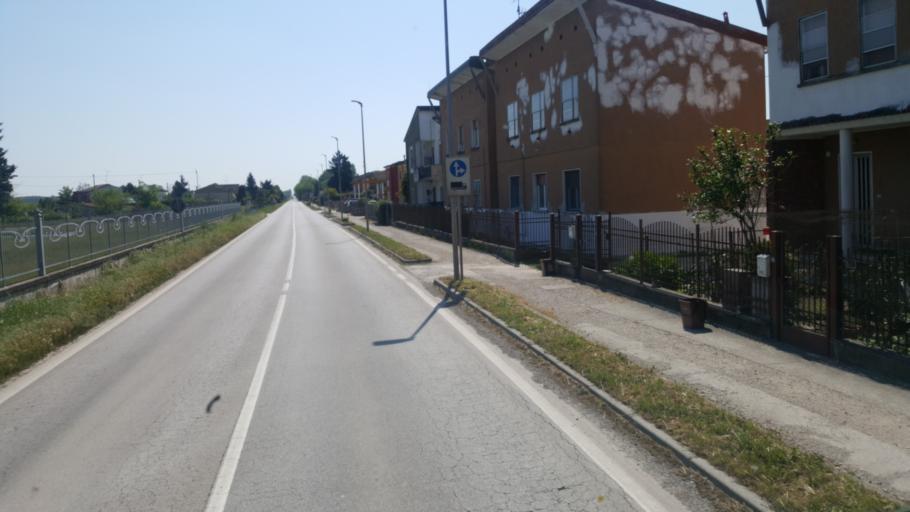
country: IT
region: Lombardy
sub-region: Provincia di Mantova
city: San Benedetto Po
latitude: 45.0874
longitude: 10.9608
